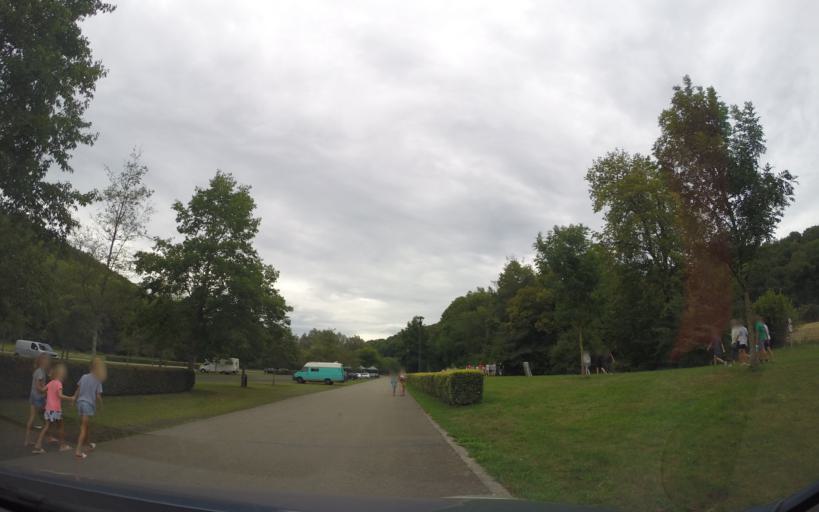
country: BE
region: Wallonia
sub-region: Province du Luxembourg
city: Durbuy
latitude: 50.3469
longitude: 5.4423
